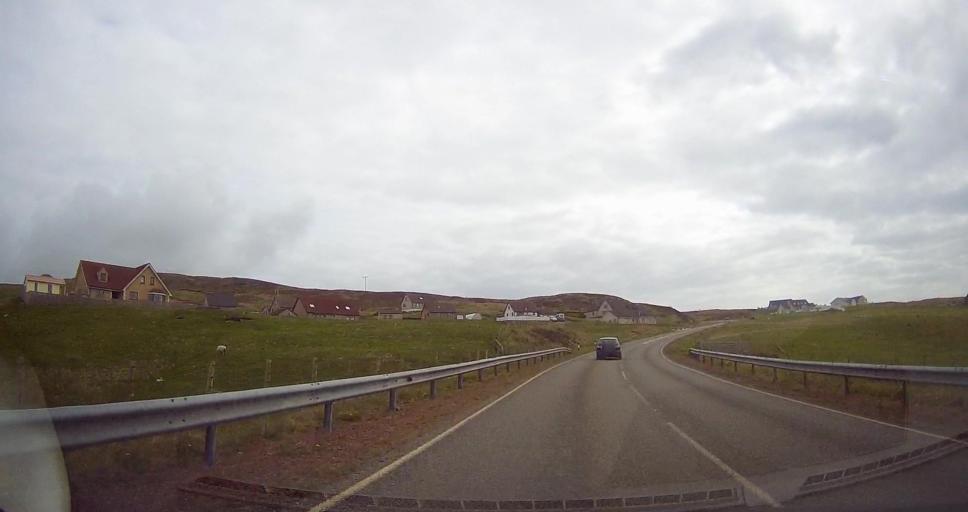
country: GB
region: Scotland
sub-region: Shetland Islands
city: Lerwick
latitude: 60.1045
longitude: -1.2297
